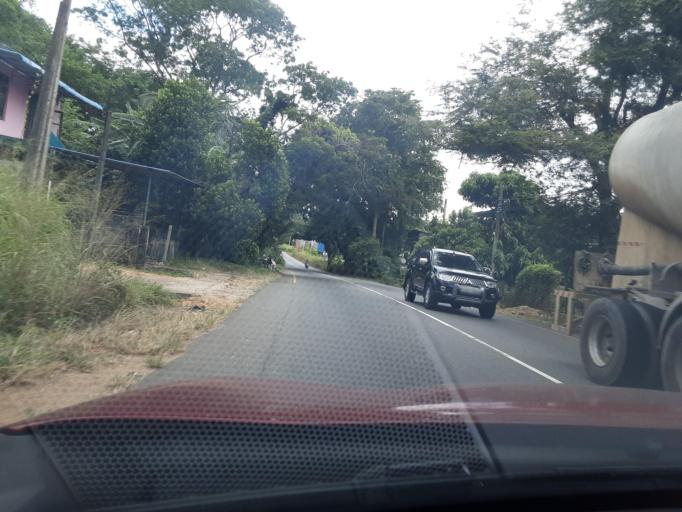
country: LK
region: North Western
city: Kurunegala
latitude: 7.4394
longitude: 80.2400
